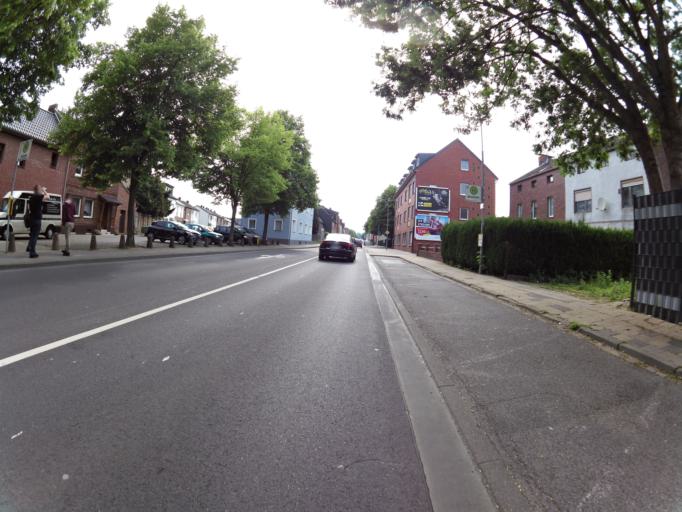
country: DE
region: North Rhine-Westphalia
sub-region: Regierungsbezirk Koln
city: Alsdorf
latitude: 50.8750
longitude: 6.1794
